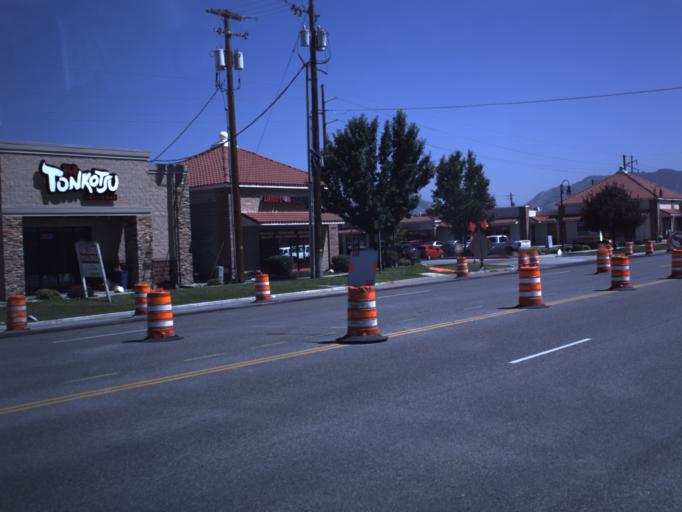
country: US
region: Utah
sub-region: Salt Lake County
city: Taylorsville
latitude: 40.6965
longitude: -111.9430
